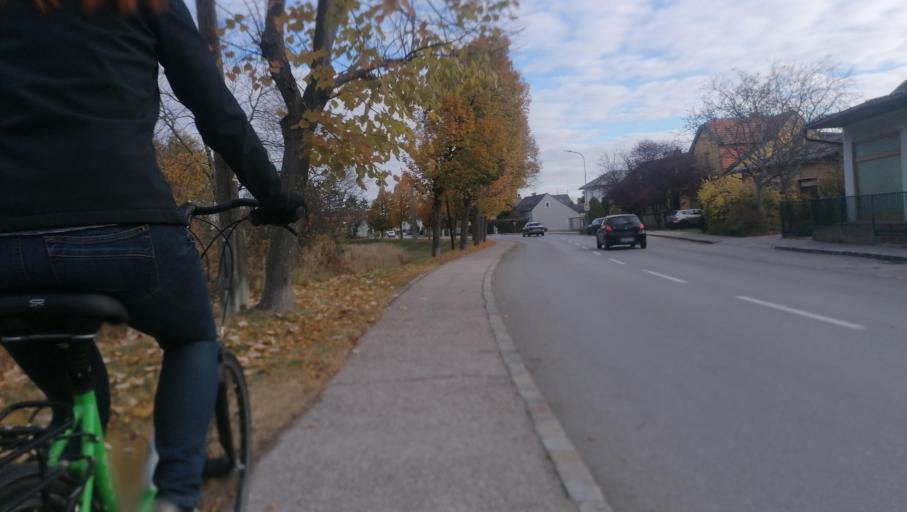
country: AT
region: Lower Austria
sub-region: Politischer Bezirk Baden
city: Oberwaltersdorf
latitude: 47.9714
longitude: 16.3207
